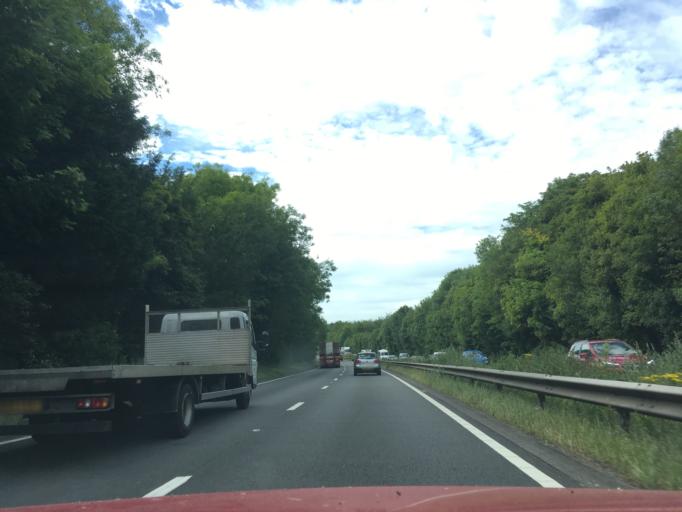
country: GB
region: England
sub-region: Hampshire
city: Kings Worthy
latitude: 51.0894
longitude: -1.3033
